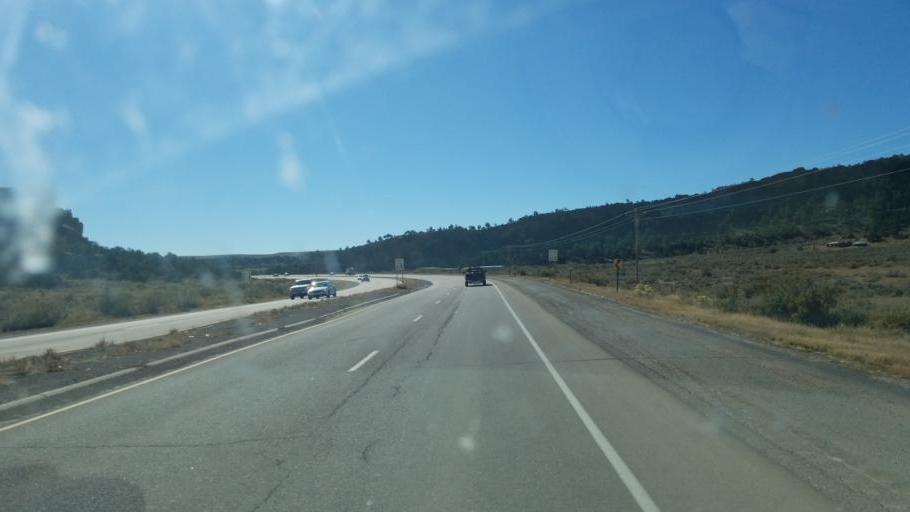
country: US
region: Arizona
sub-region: Apache County
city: Window Rock
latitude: 35.6539
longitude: -109.0395
